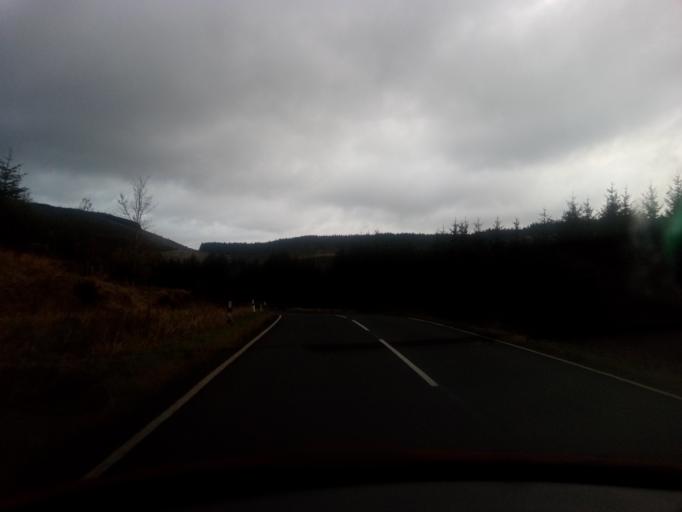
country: GB
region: Scotland
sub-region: The Scottish Borders
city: Hawick
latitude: 55.3083
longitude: -2.6570
